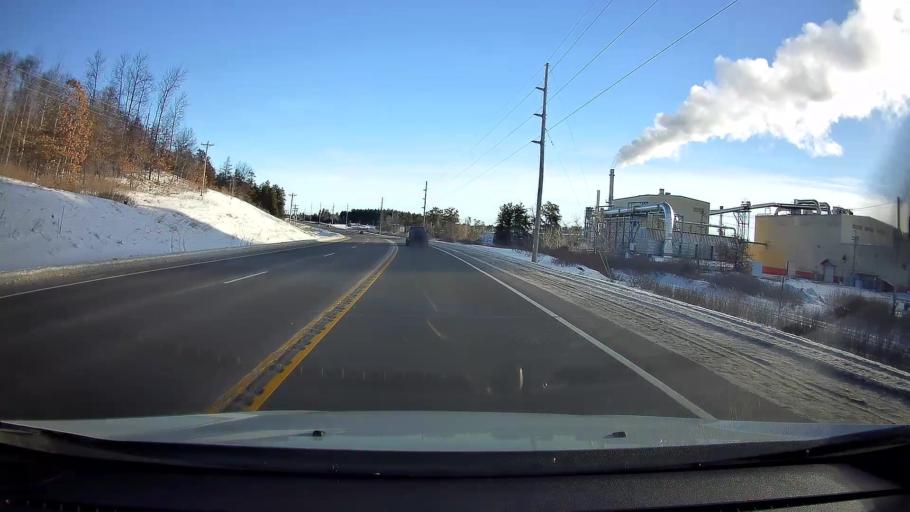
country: US
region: Wisconsin
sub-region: Sawyer County
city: Hayward
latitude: 45.9865
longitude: -91.5266
